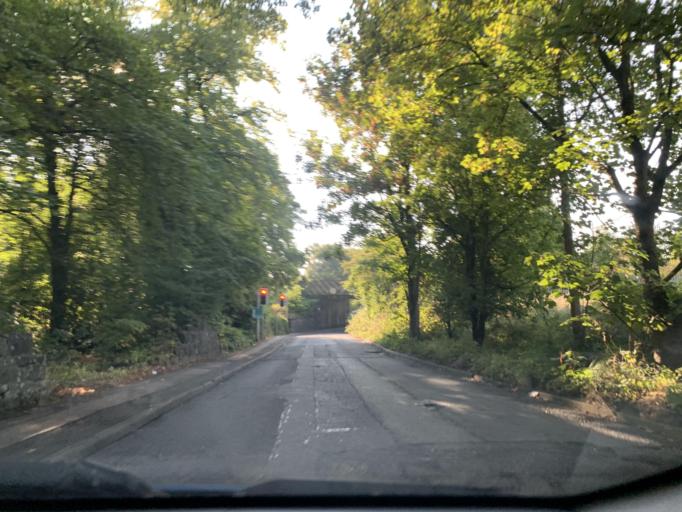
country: GB
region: Scotland
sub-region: East Renfrewshire
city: Giffnock
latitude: 55.8135
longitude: -4.3266
